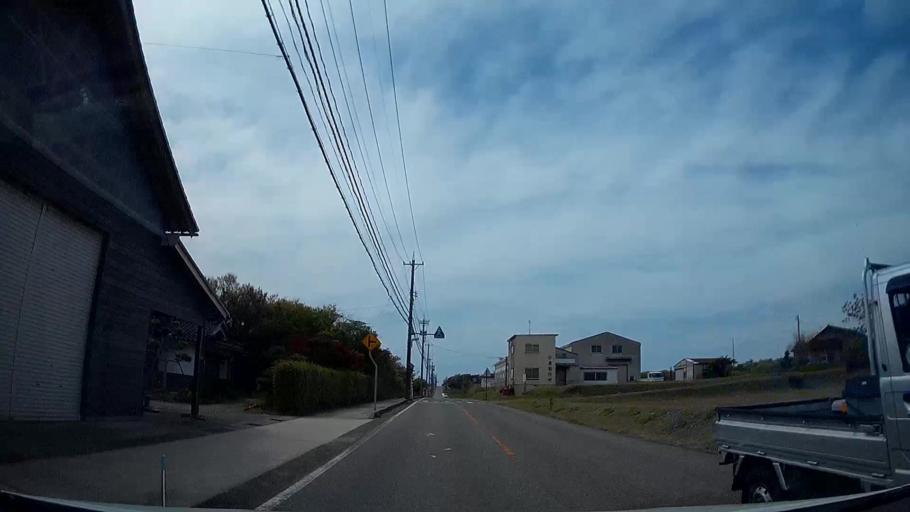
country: JP
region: Ishikawa
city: Hakui
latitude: 37.0135
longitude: 136.7570
